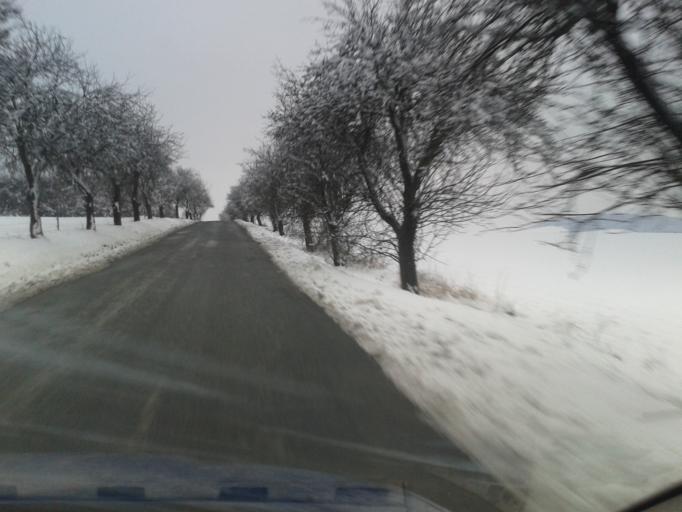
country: CZ
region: Central Bohemia
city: Revnice
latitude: 49.9218
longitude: 14.1648
